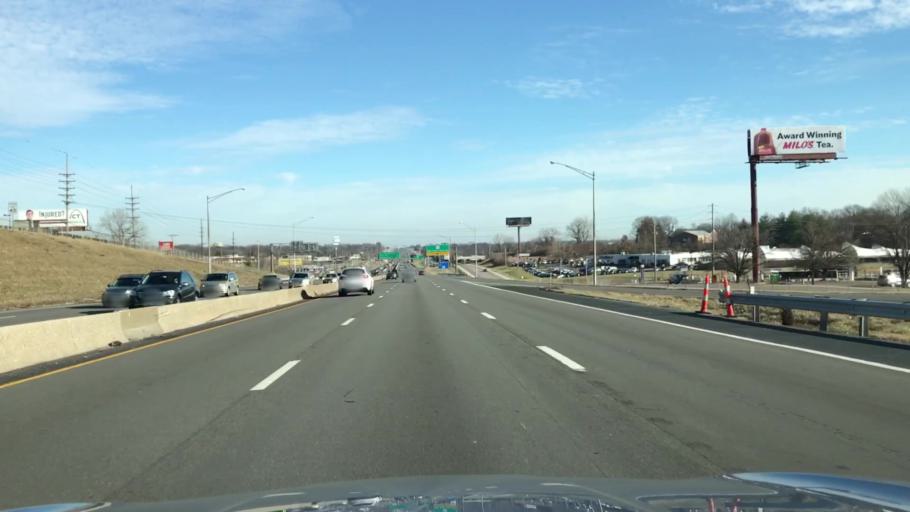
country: US
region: Missouri
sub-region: Saint Louis County
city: Dellwood
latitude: 38.7711
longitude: -90.2769
